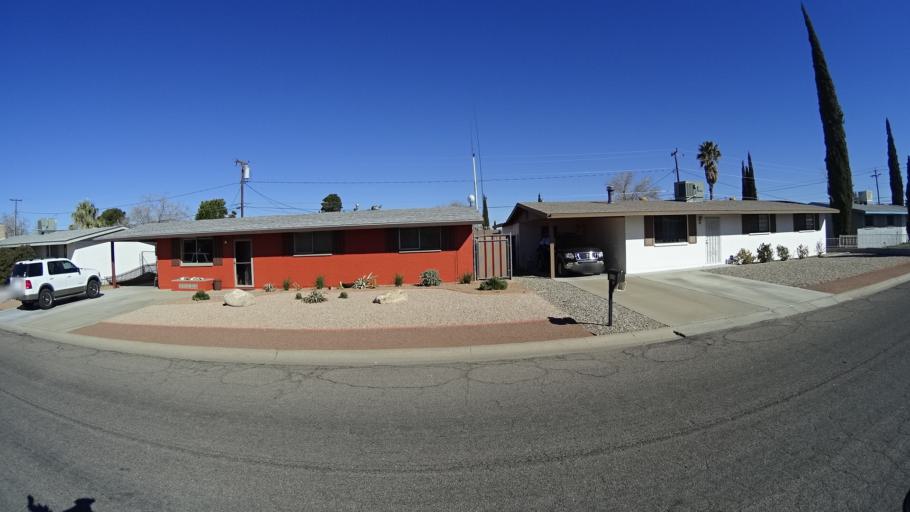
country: US
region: Arizona
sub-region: Mohave County
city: Kingman
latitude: 35.2089
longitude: -114.0298
